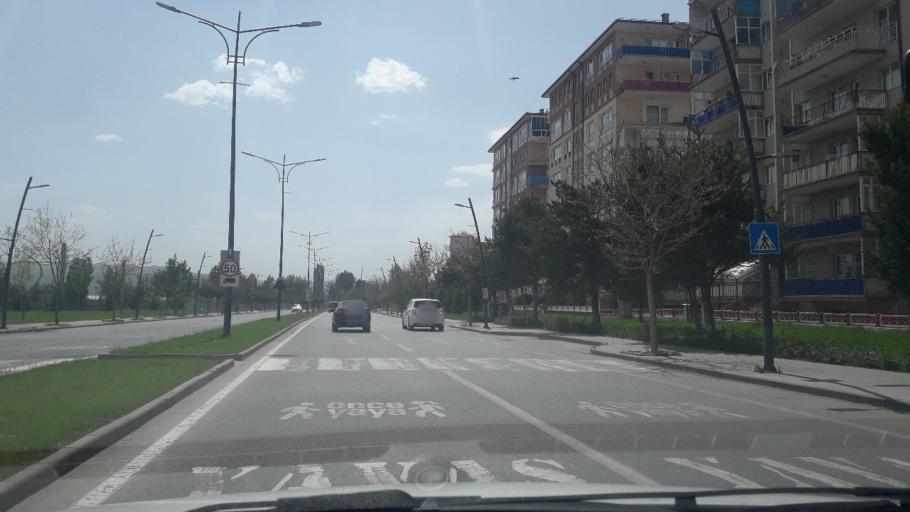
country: TR
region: Sivas
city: Sivas
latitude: 39.7279
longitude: 36.9760
